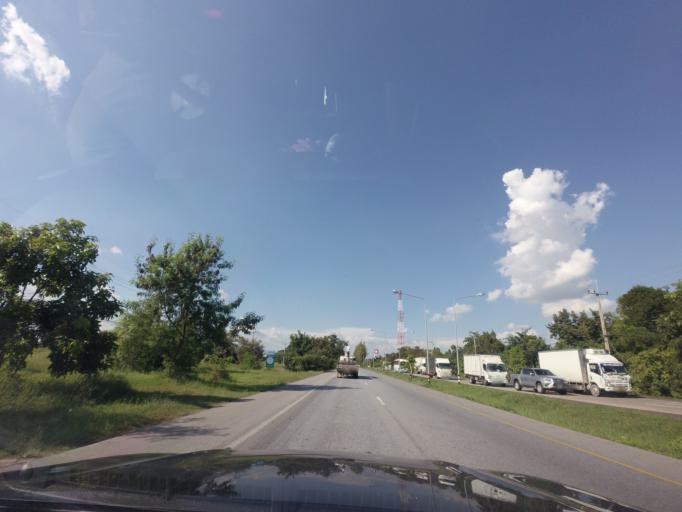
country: TH
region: Nakhon Ratchasima
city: Sida
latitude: 15.5349
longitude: 102.5448
